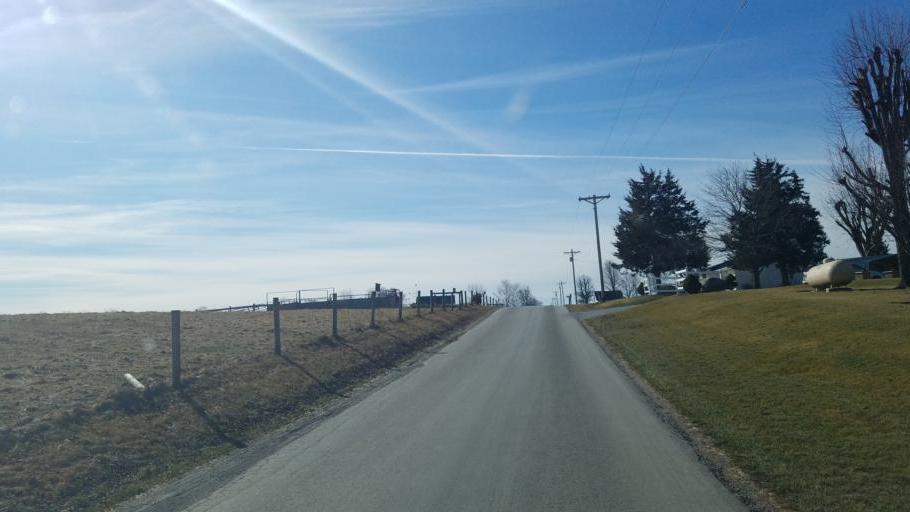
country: US
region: Ohio
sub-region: Hardin County
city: Kenton
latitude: 40.5903
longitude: -83.4502
